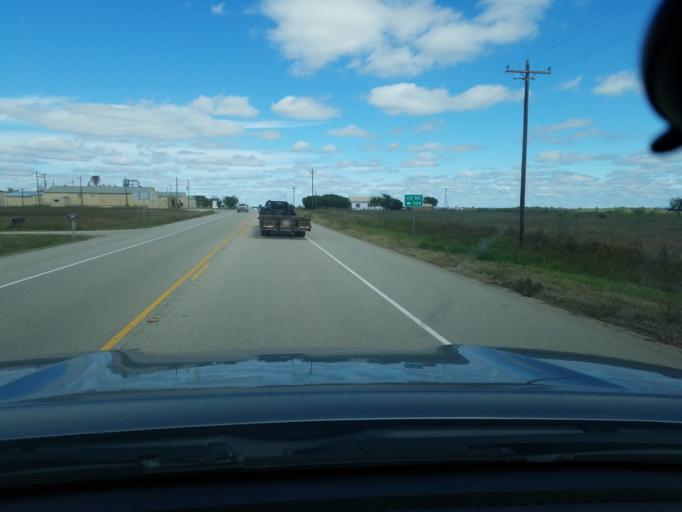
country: US
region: Texas
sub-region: Hamilton County
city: Hamilton
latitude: 31.6675
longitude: -98.1390
